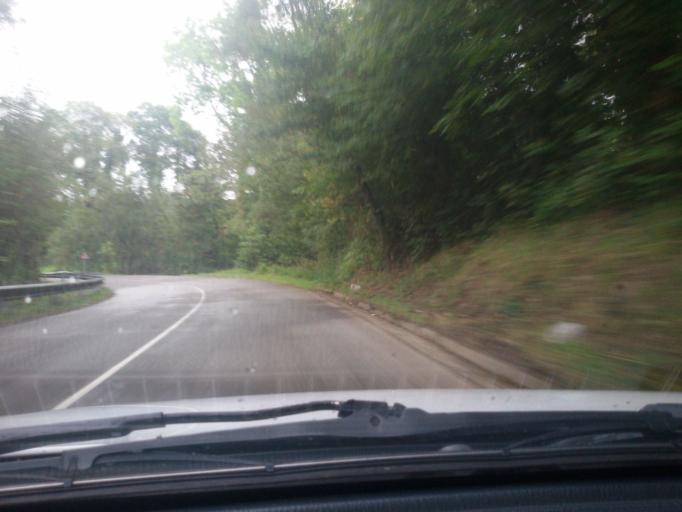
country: ES
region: Asturias
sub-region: Province of Asturias
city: Norena
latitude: 43.3715
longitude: -5.7377
